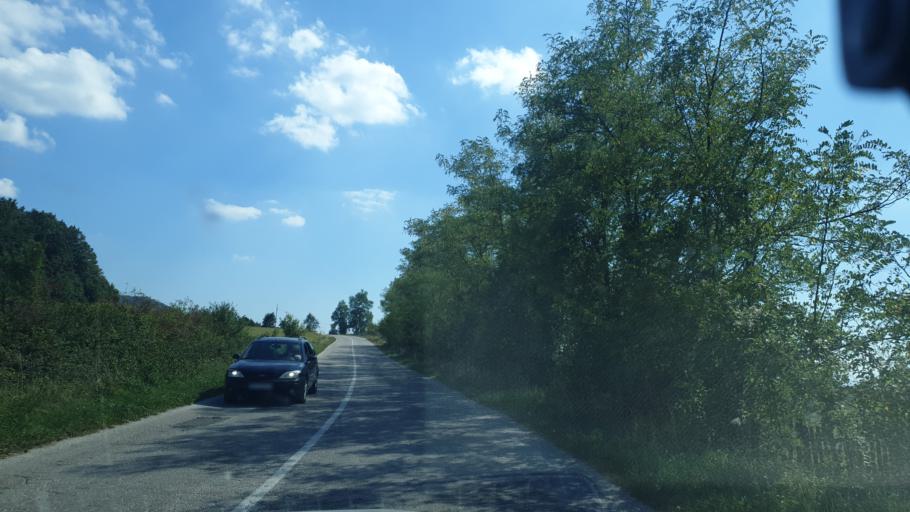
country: RS
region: Central Serbia
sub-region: Zlatiborski Okrug
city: Kosjeric
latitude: 44.0213
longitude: 20.0248
